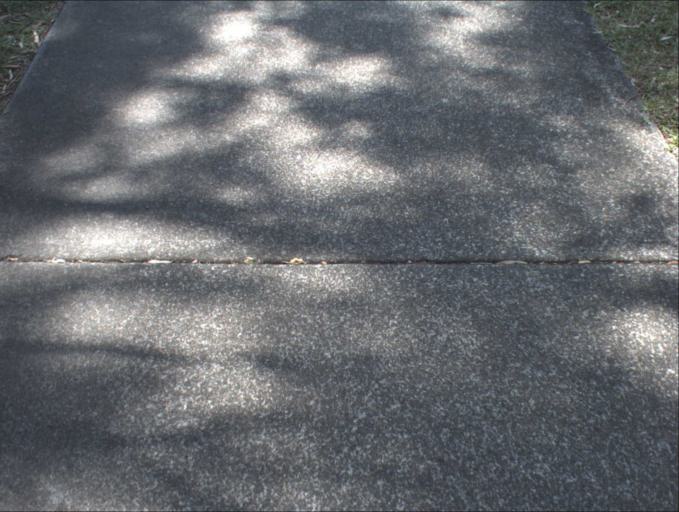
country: AU
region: Queensland
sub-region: Logan
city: Rochedale South
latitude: -27.6085
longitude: 153.1055
